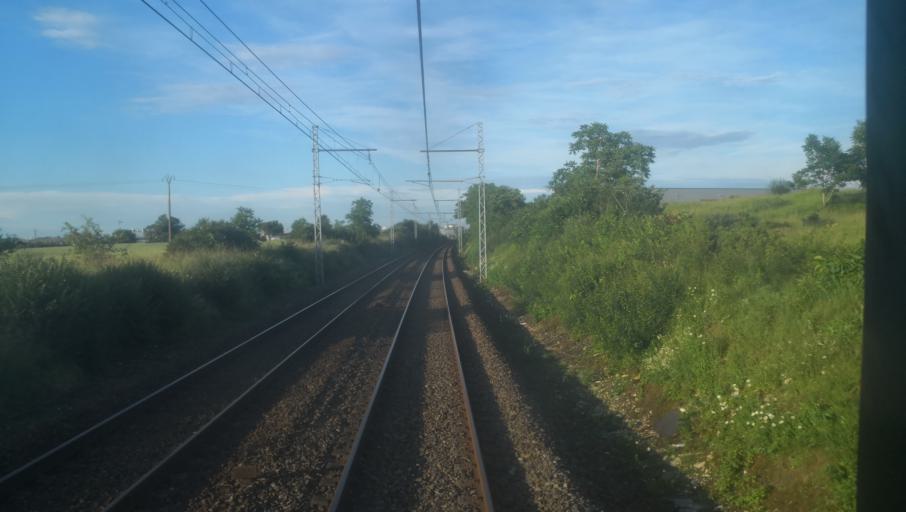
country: FR
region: Centre
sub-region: Departement de l'Indre
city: Saint-Maur
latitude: 46.7925
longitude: 1.6588
